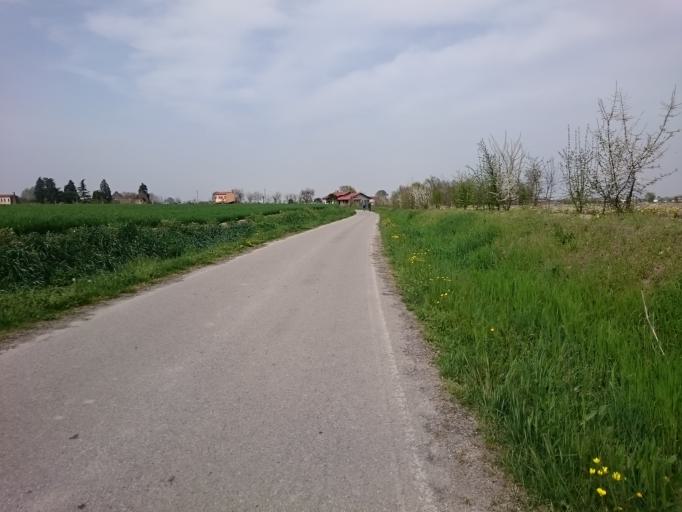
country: IT
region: Veneto
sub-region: Provincia di Padova
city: Tribano
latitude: 45.1885
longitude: 11.8325
